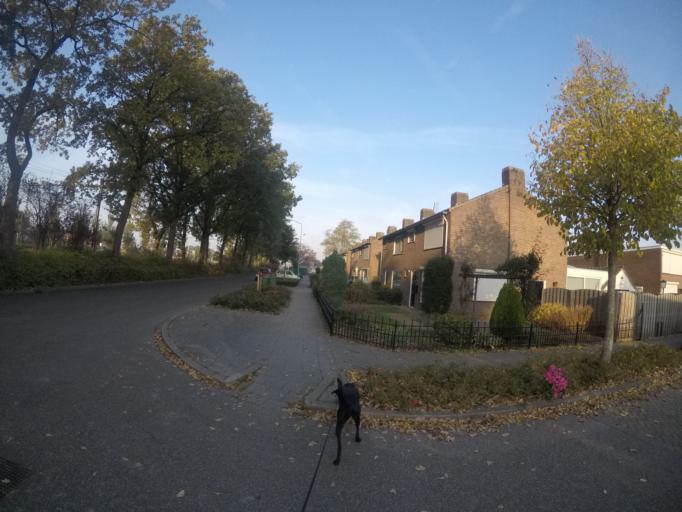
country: NL
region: Gelderland
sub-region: Gemeente Zevenaar
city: Zevenaar
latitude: 51.9248
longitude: 6.0666
